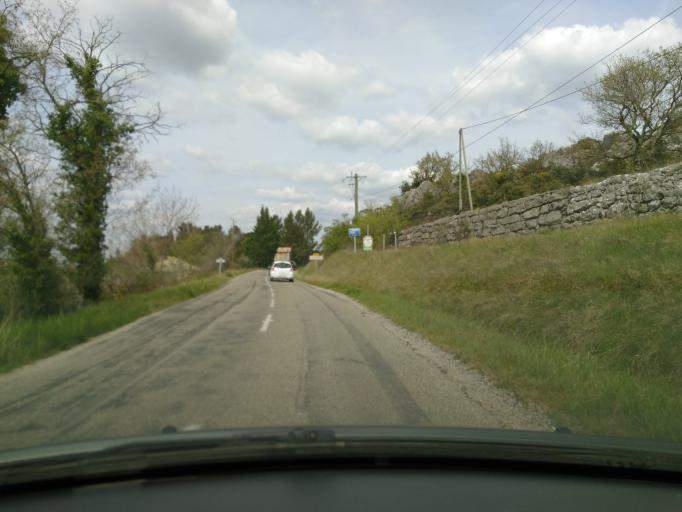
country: FR
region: Rhone-Alpes
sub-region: Departement de l'Ardeche
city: Ruoms
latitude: 44.4437
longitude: 4.4147
